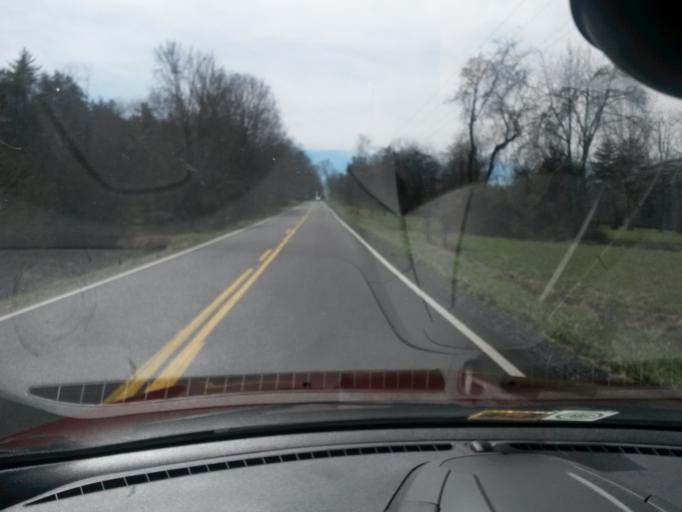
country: US
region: West Virginia
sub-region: Greenbrier County
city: White Sulphur Springs
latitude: 37.6985
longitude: -80.2154
